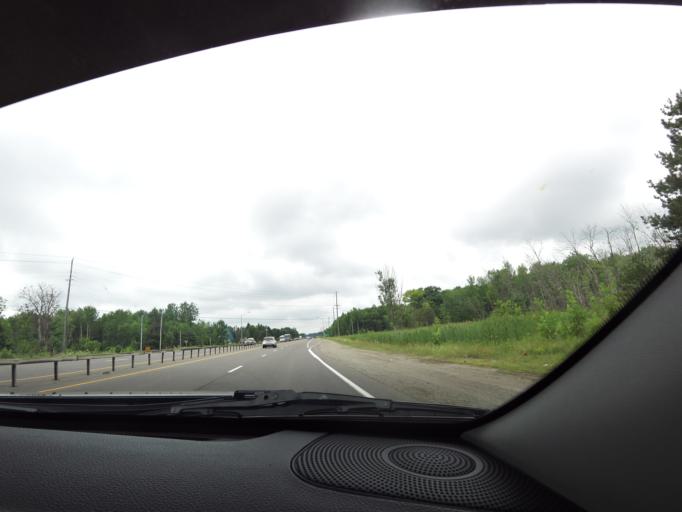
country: CA
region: Ontario
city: Orillia
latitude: 44.7425
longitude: -79.3471
